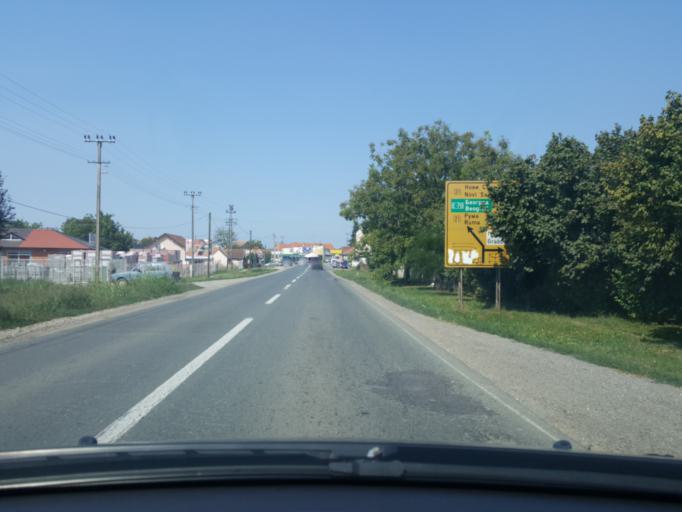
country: RS
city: Platicevo
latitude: 44.8218
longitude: 19.7801
